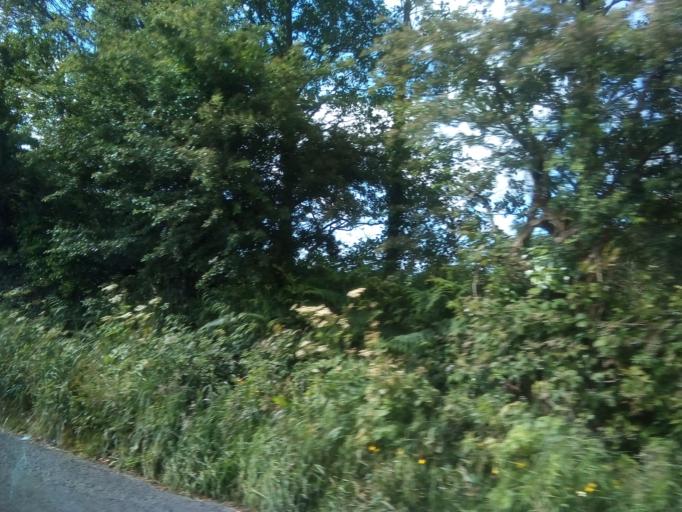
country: IE
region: Leinster
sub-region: Loch Garman
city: Loch Garman
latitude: 52.2642
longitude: -6.5574
